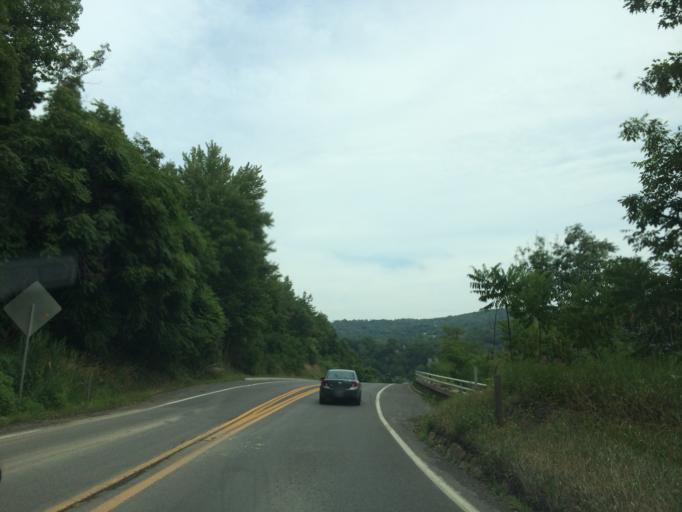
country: US
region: Maryland
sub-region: Allegany County
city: Westernport
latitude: 39.4837
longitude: -79.0503
